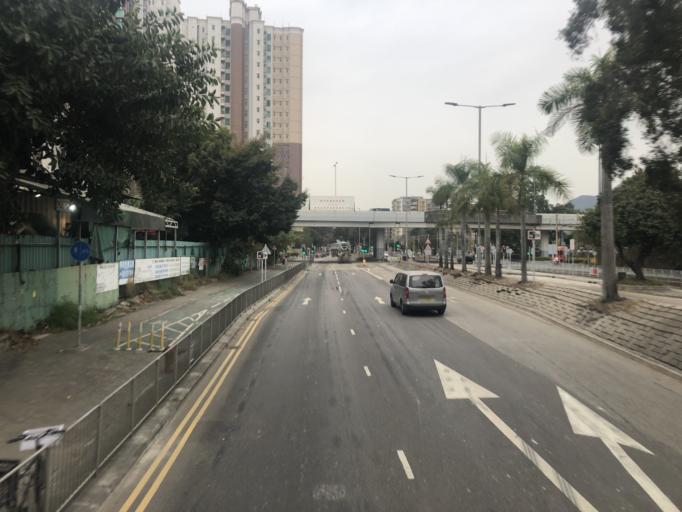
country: HK
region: Yuen Long
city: Yuen Long Kau Hui
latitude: 22.4363
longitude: 114.0015
